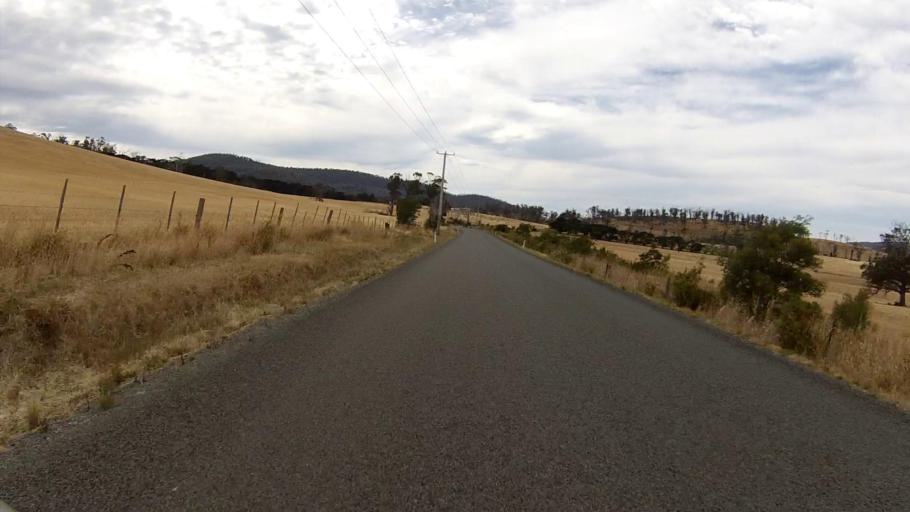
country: AU
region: Tasmania
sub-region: Sorell
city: Sorell
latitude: -42.8984
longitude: 147.7681
